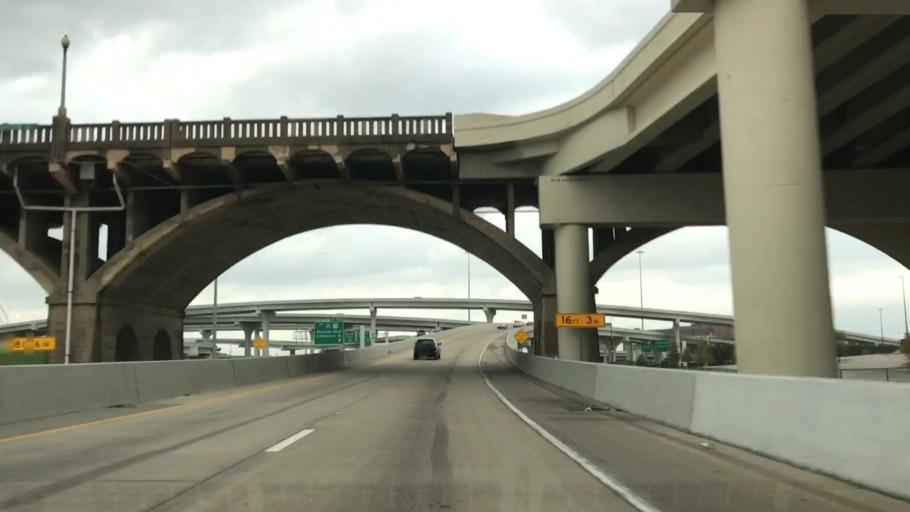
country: US
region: Texas
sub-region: Dallas County
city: Dallas
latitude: 32.7706
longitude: -96.8079
